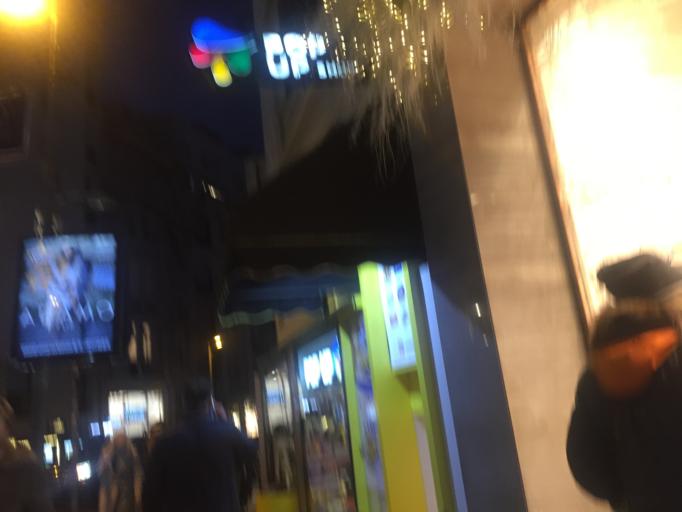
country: TR
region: Istanbul
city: Sisli
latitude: 41.0485
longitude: 28.9945
